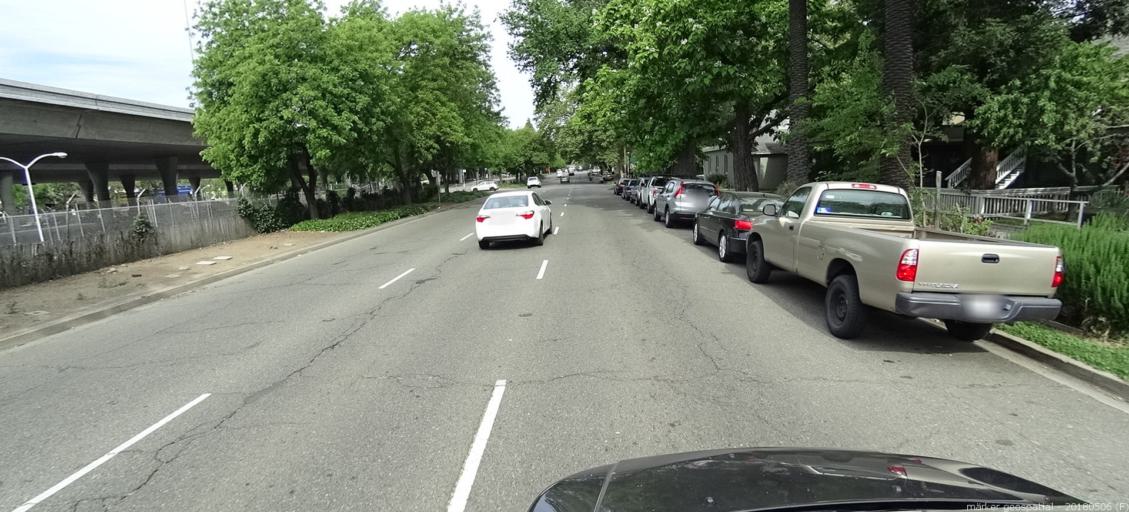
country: US
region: California
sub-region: Sacramento County
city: Sacramento
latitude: 38.5614
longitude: -121.4825
